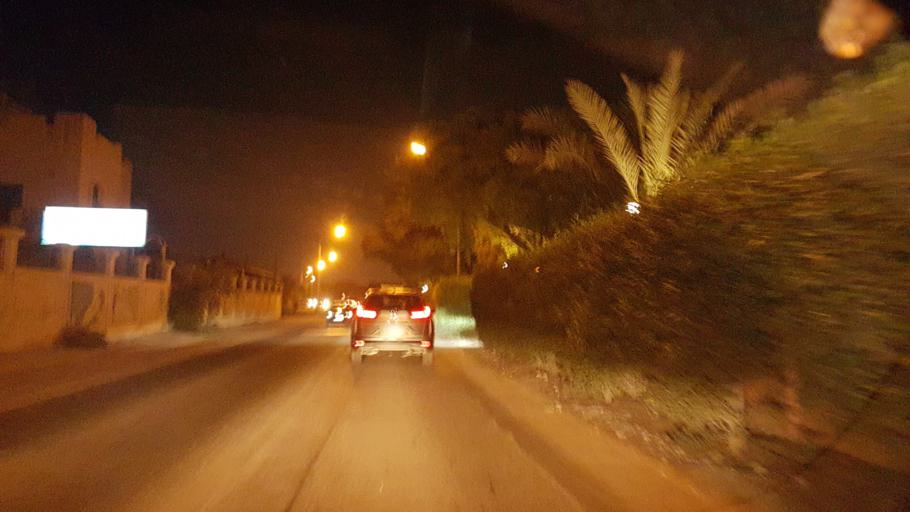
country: BH
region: Manama
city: Jidd Hafs
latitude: 26.2311
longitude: 50.4980
